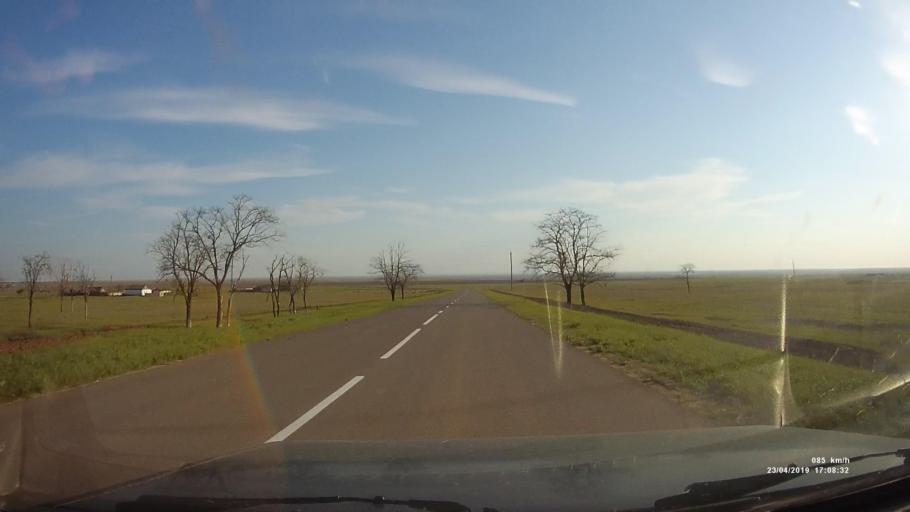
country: RU
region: Kalmykiya
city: Priyutnoye
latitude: 46.2699
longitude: 43.4868
